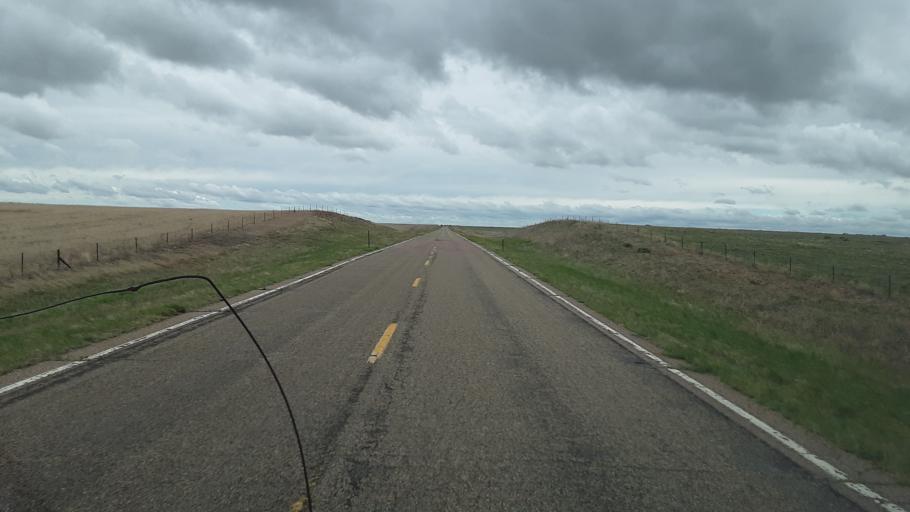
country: US
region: Colorado
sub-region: Lincoln County
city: Hugo
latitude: 38.8515
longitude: -103.6466
